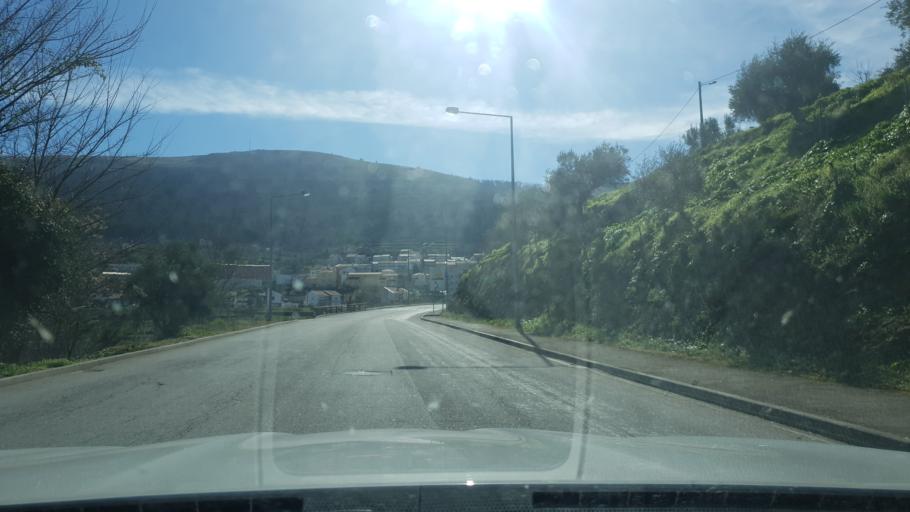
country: PT
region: Braganca
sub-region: Torre de Moncorvo
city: Torre de Moncorvo
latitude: 41.1778
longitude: -7.0506
